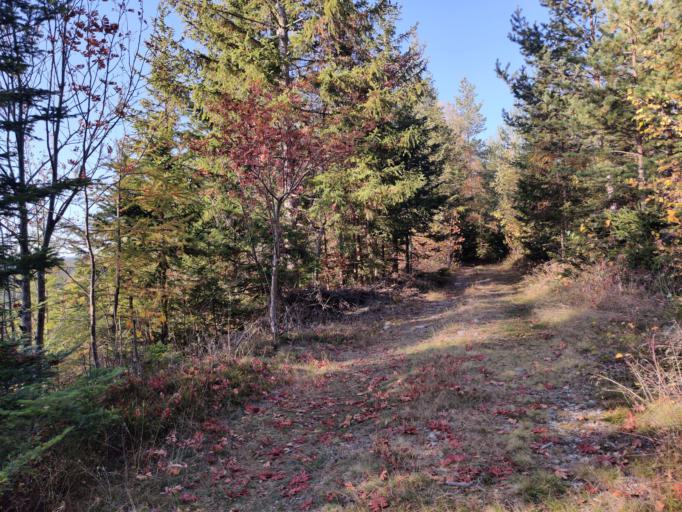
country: AT
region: Styria
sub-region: Politischer Bezirk Hartberg-Fuerstenfeld
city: Sankt Jakob im Walde
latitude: 47.4674
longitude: 15.8159
